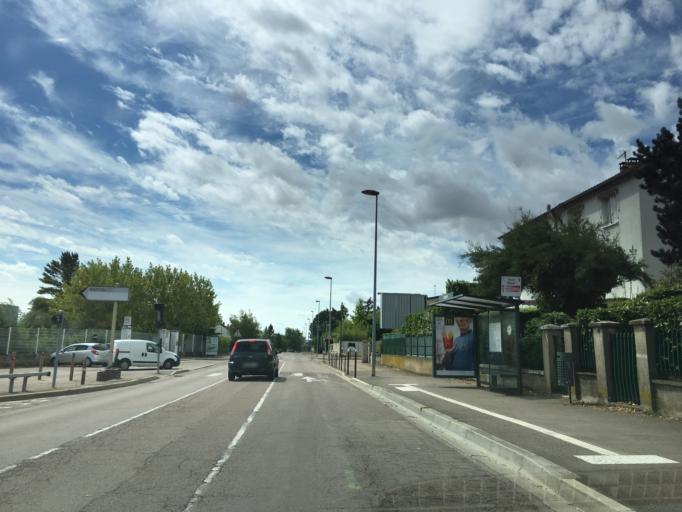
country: FR
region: Bourgogne
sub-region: Departement de l'Yonne
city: Auxerre
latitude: 47.8029
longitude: 3.5530
